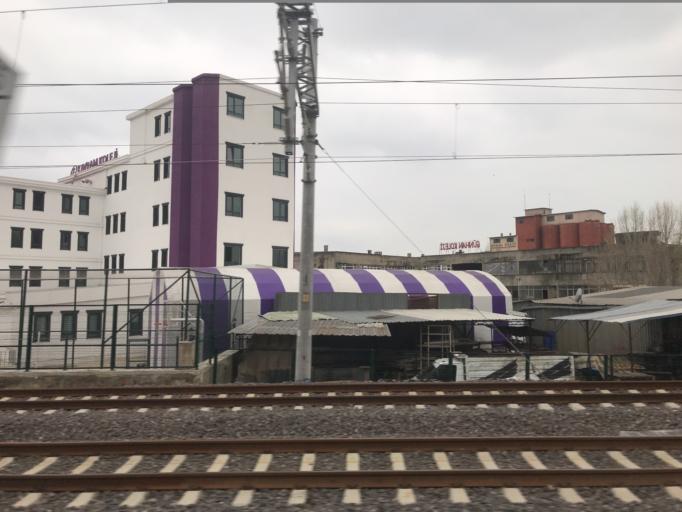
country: TR
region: Istanbul
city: Maltepe
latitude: 40.9166
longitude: 29.1430
